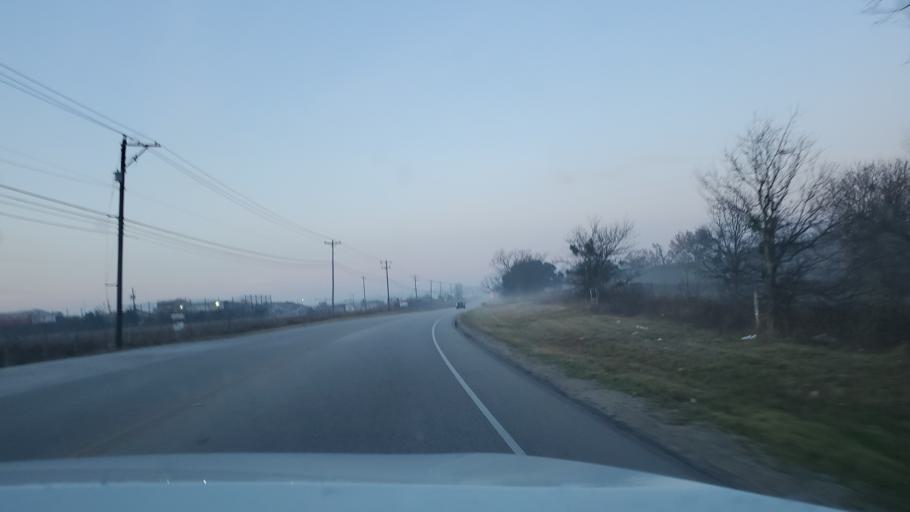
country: US
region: Texas
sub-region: Travis County
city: Garfield
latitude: 30.1733
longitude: -97.6515
